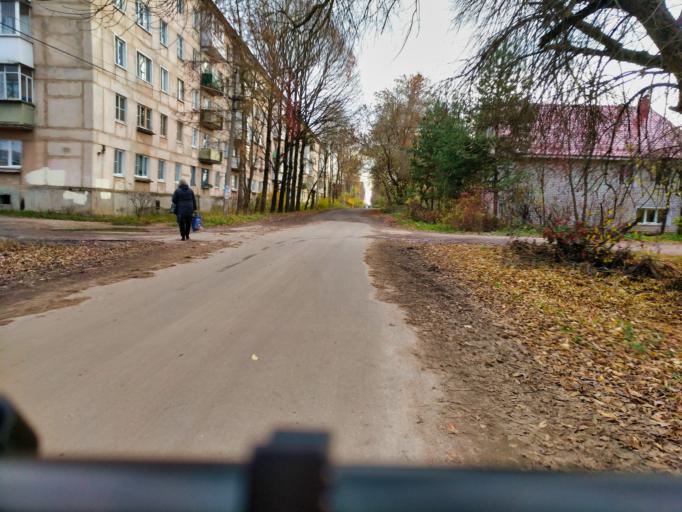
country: RU
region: Tverskaya
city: Rzhev
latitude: 56.2689
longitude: 34.3262
